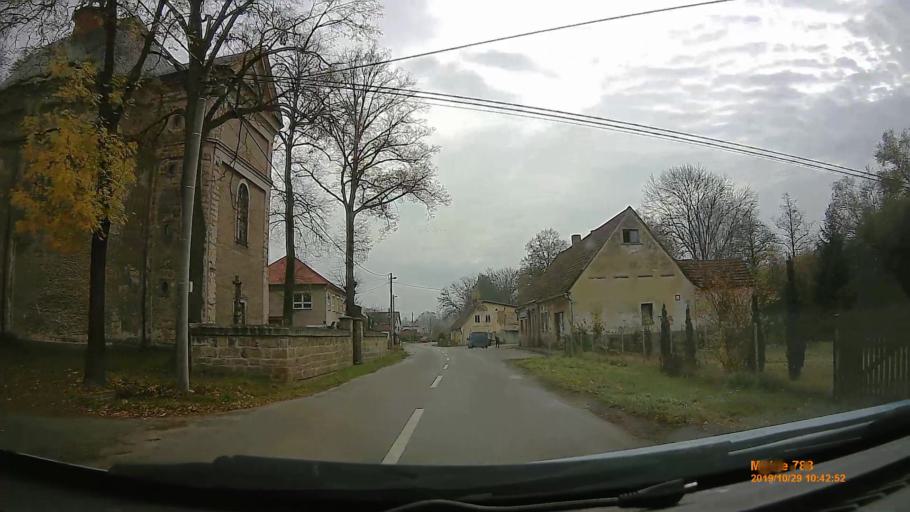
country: PL
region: Lower Silesian Voivodeship
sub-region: Powiat klodzki
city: Radkow
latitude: 50.5575
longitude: 16.3849
